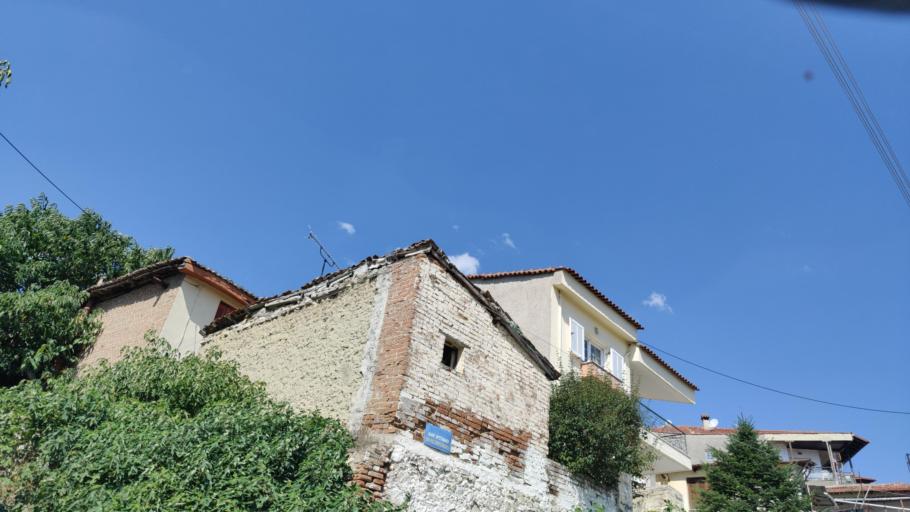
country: GR
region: Central Macedonia
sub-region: Nomos Serron
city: Serres
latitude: 41.0895
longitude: 23.5384
